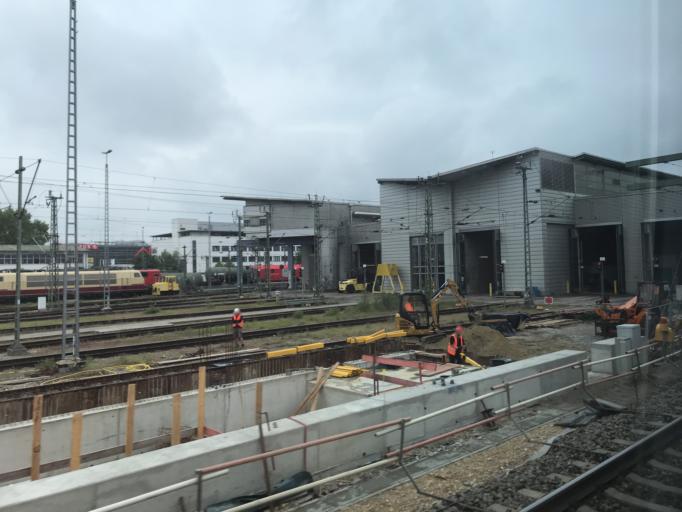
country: DE
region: Bavaria
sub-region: Upper Bavaria
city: Munich
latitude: 48.1426
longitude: 11.5271
